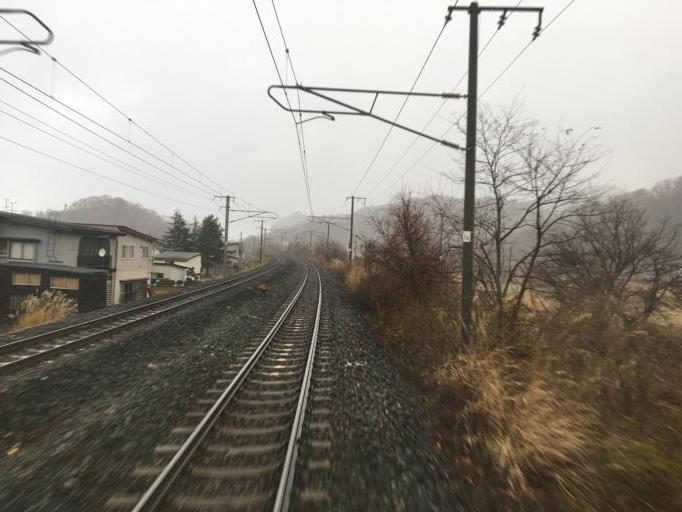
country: JP
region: Aomori
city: Aomori Shi
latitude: 40.8498
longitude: 140.8209
